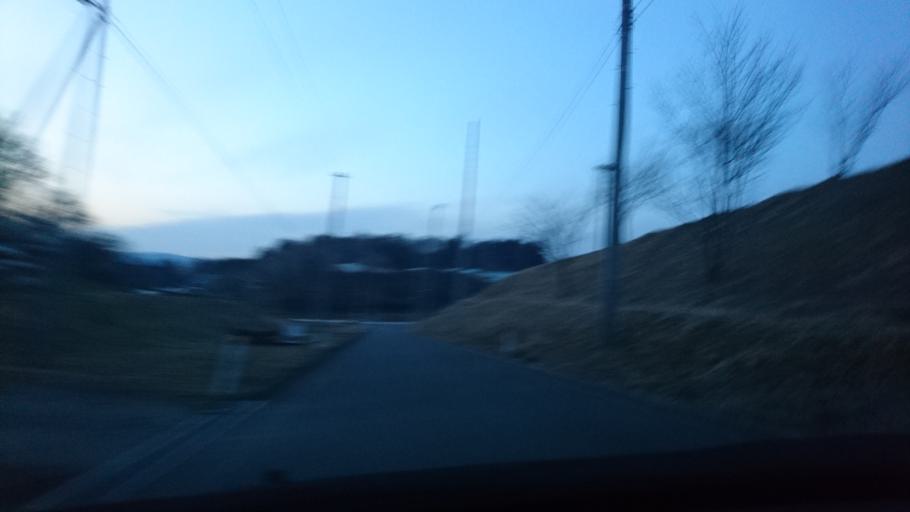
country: JP
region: Iwate
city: Ichinoseki
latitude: 38.9095
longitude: 141.3463
